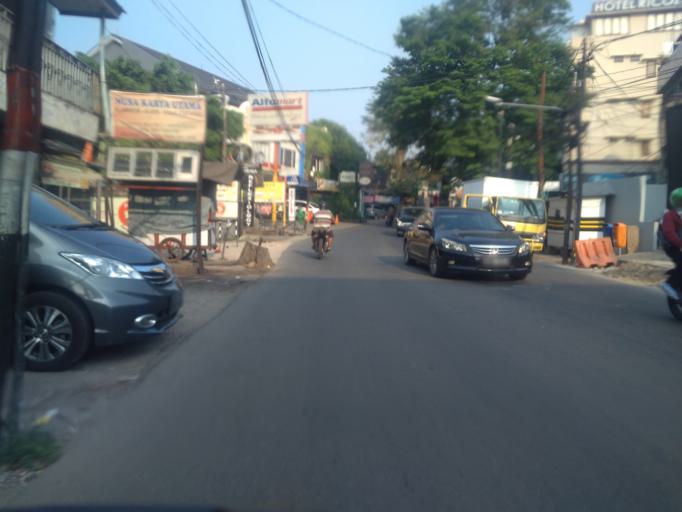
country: ID
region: Jakarta Raya
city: Jakarta
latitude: -6.2640
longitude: 106.7970
